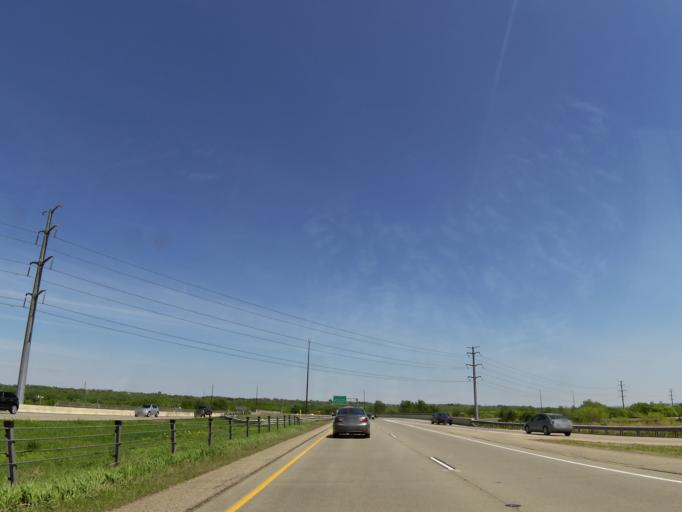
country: US
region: Minnesota
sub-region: Scott County
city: Prior Lake
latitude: 44.7866
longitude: -93.4115
